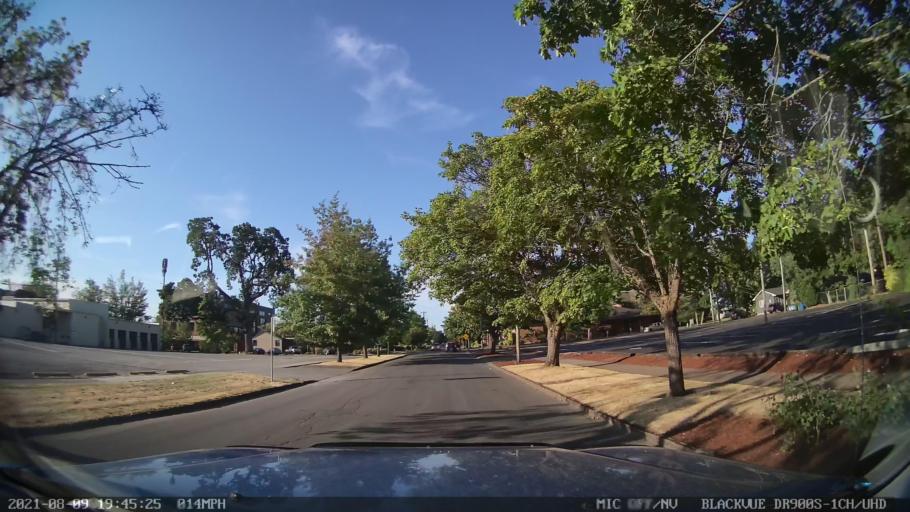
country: US
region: Oregon
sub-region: Marion County
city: Salem
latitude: 44.9508
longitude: -123.0301
